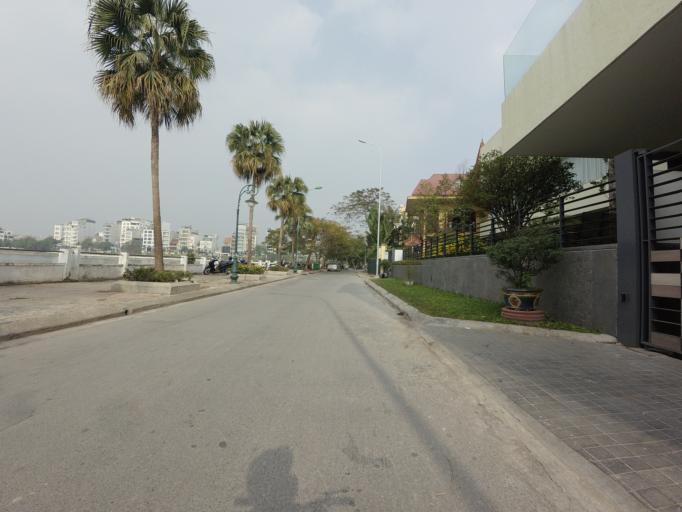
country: VN
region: Ha Noi
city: Tay Ho
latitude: 21.0591
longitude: 105.8297
